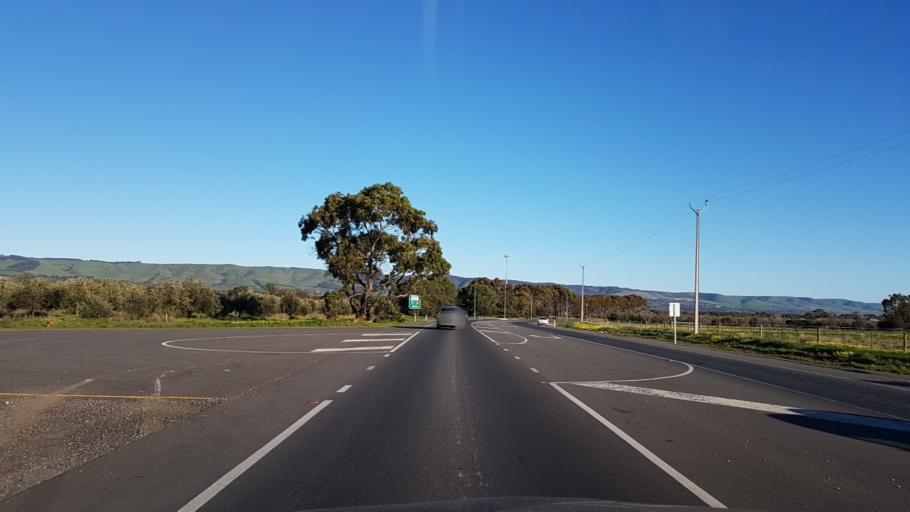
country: AU
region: South Australia
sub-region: Onkaparinga
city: Aldinga
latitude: -35.2512
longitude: 138.4947
